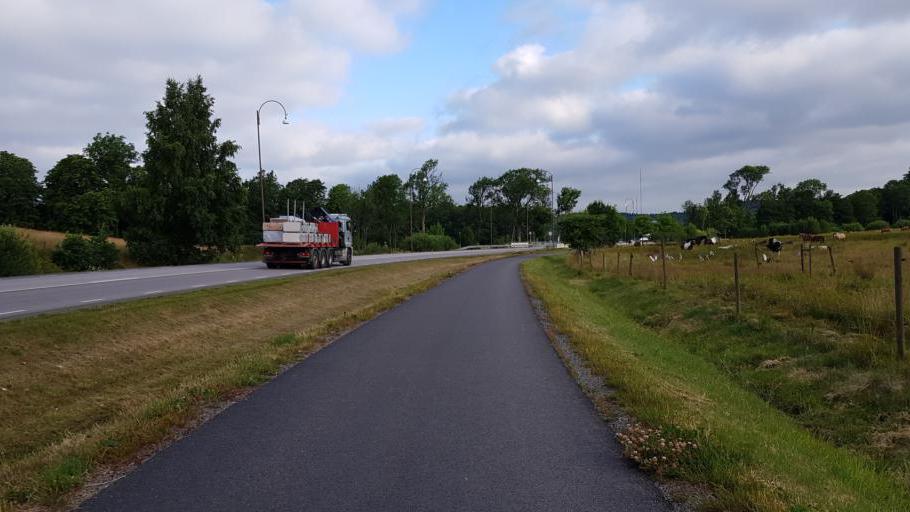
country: SE
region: Vaestra Goetaland
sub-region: Harryda Kommun
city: Molnlycke
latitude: 57.6608
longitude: 12.0938
